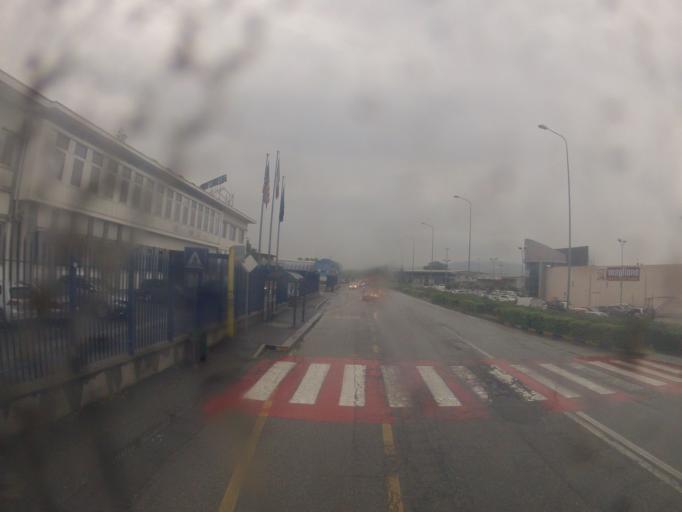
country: IT
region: Piedmont
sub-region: Provincia di Torino
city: La Loggia
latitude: 44.9631
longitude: 7.6684
